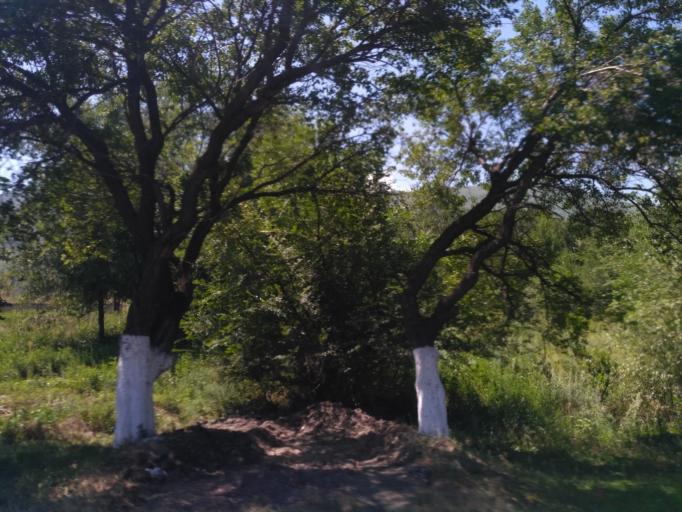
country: KZ
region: Almaty Oblysy
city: Burunday
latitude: 43.1668
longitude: 76.5700
